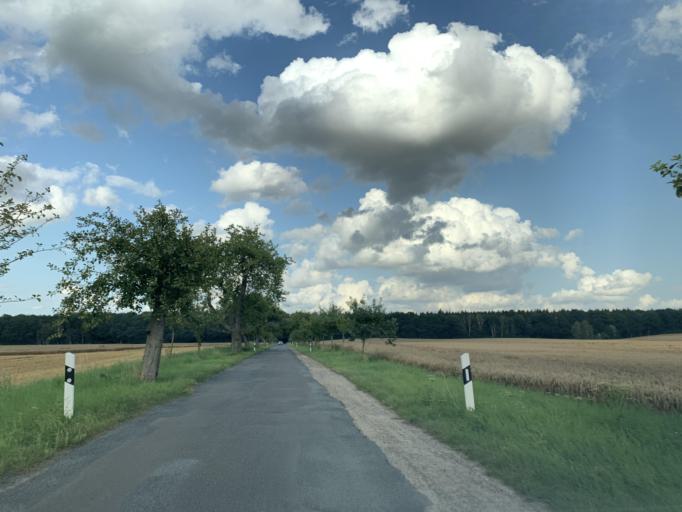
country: DE
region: Mecklenburg-Vorpommern
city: Gross Nemerow
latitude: 53.4691
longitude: 13.2718
